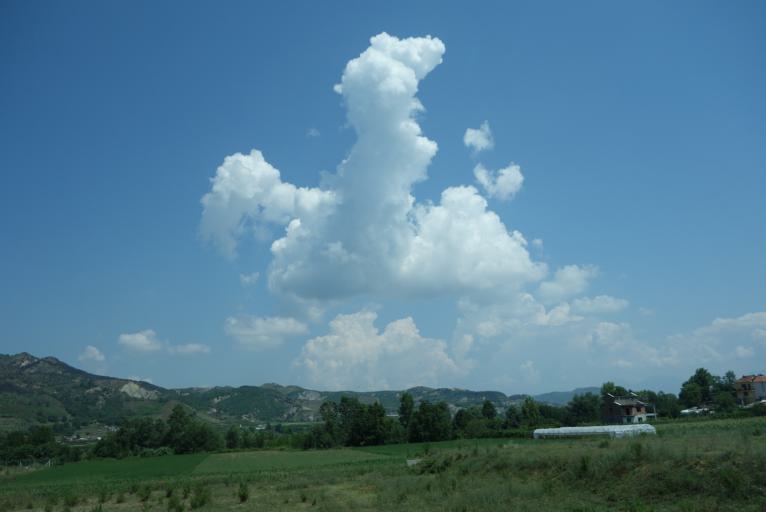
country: AL
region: Tirane
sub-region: Rrethi i Tiranes
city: Ndroq
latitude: 41.2595
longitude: 19.6800
